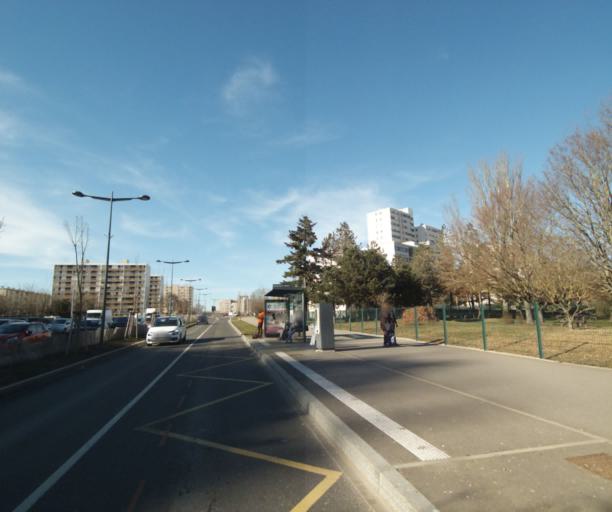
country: FR
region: Lorraine
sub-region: Departement de Meurthe-et-Moselle
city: Vandoeuvre-les-Nancy
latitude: 48.6632
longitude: 6.1758
